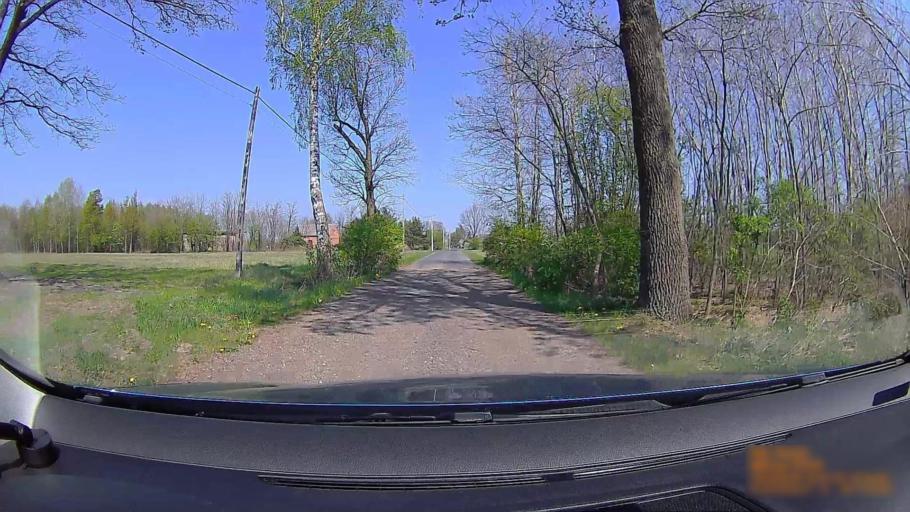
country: PL
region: Greater Poland Voivodeship
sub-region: Powiat koninski
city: Rychwal
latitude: 52.0952
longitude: 18.1835
